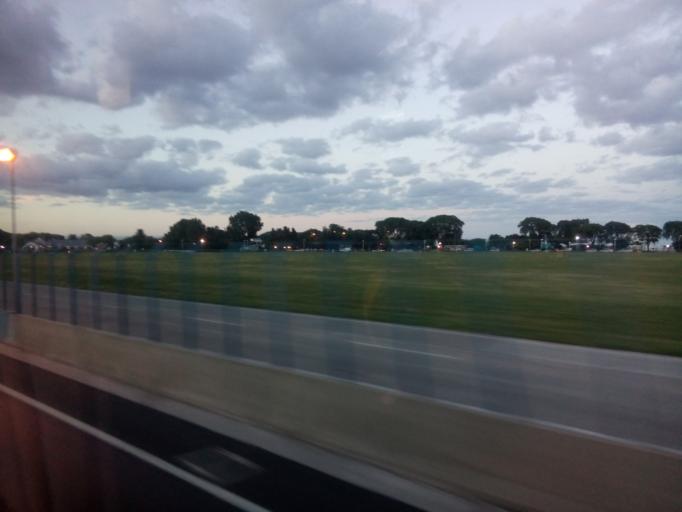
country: AR
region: Buenos Aires F.D.
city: Colegiales
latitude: -34.5531
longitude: -58.4293
